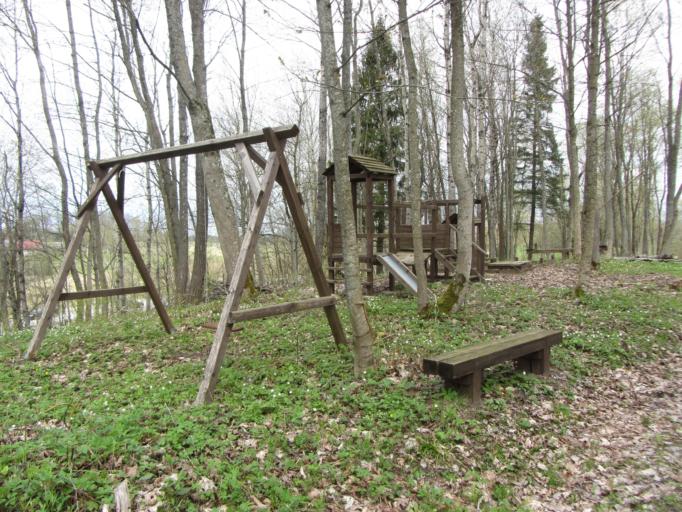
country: LT
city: Moletai
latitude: 55.1447
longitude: 25.4064
